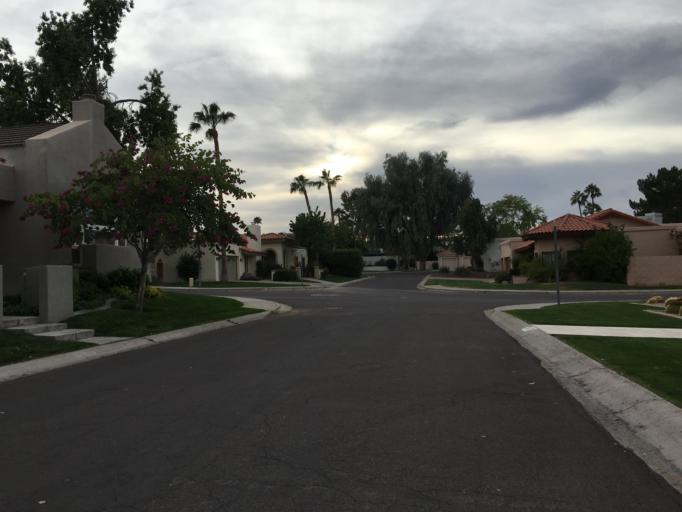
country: US
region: Arizona
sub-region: Maricopa County
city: Paradise Valley
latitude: 33.5700
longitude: -112.0074
